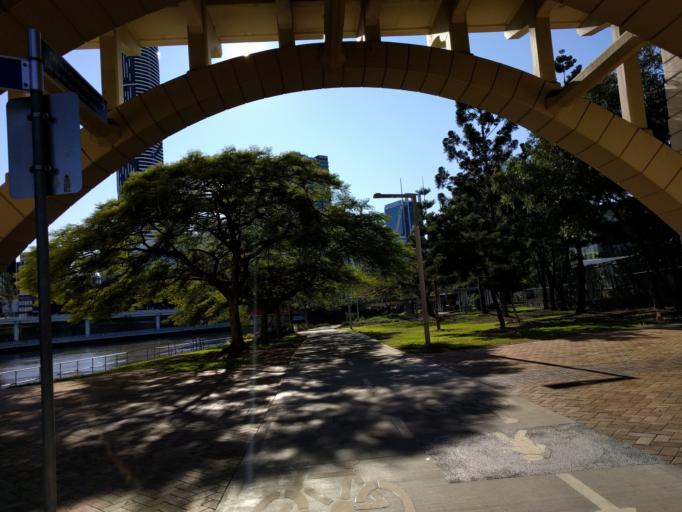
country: AU
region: Queensland
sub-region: Brisbane
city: Spring Hill
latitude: -27.4696
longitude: 153.0157
